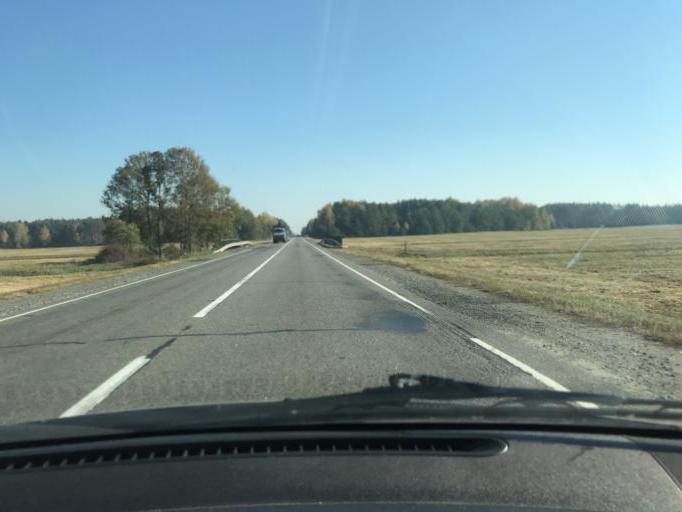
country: BY
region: Brest
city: Davyd-Haradok
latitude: 52.2462
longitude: 27.1145
